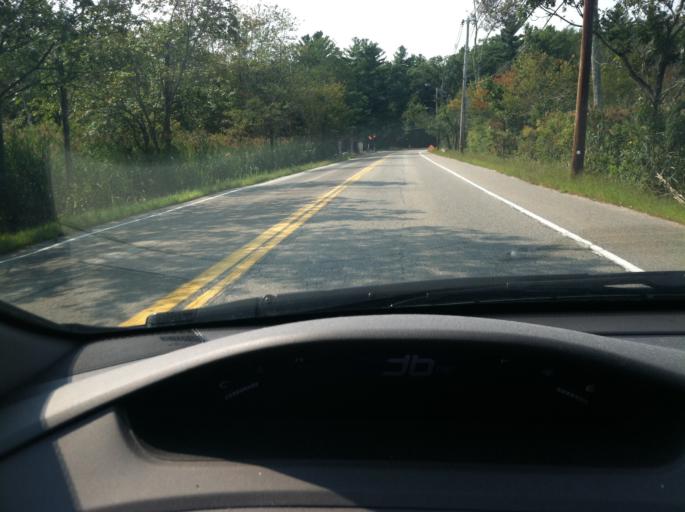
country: US
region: Massachusetts
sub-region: Middlesex County
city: Bedford
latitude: 42.4980
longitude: -71.2880
